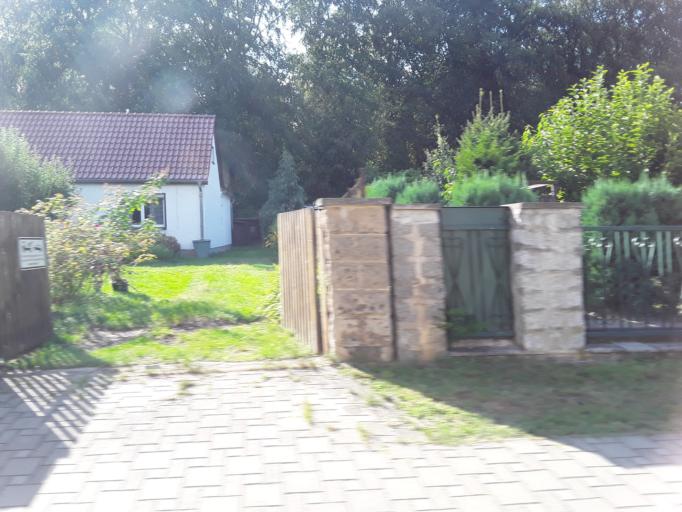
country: DE
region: Berlin
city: Buch
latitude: 52.6301
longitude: 13.5187
